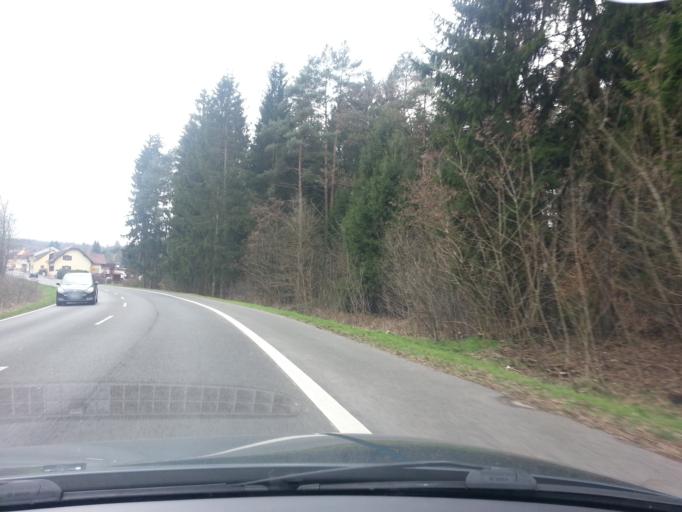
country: DE
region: Saarland
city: Bexbach
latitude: 49.3345
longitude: 7.2245
